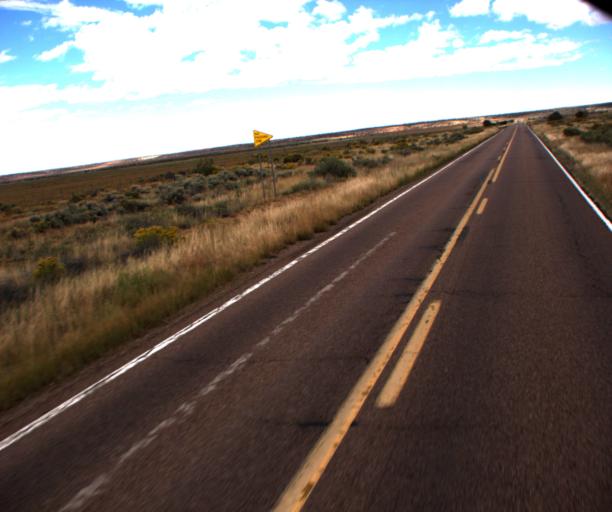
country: US
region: Arizona
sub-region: Navajo County
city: Heber-Overgaard
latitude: 34.6103
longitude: -110.3794
